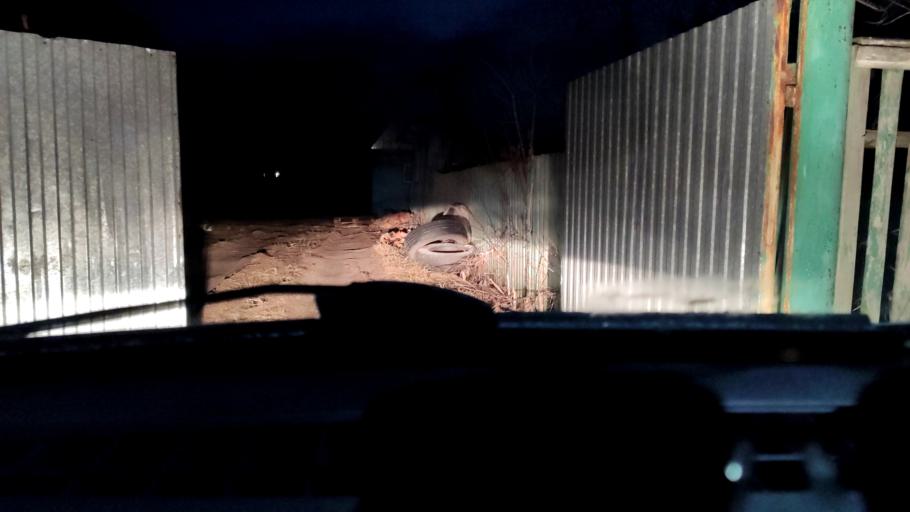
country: RU
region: Bashkortostan
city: Ulukulevo
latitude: 54.4388
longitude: 56.3079
